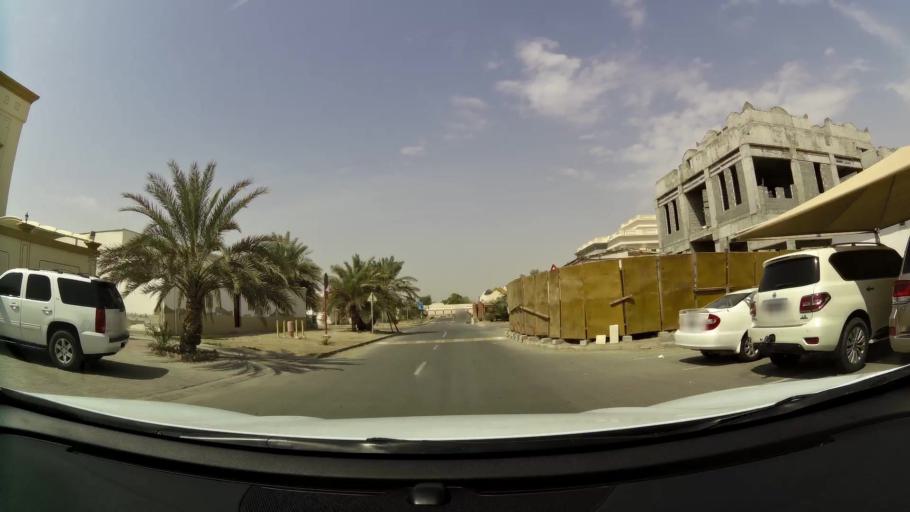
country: AE
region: Abu Dhabi
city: Abu Dhabi
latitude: 24.2957
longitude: 54.6346
